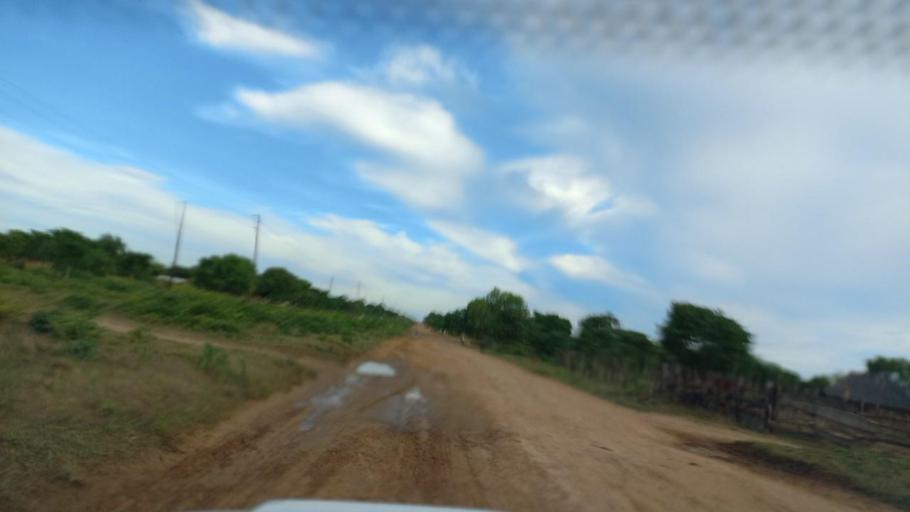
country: ZM
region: North-Western
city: Kabompo
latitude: -13.4255
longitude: 24.3256
